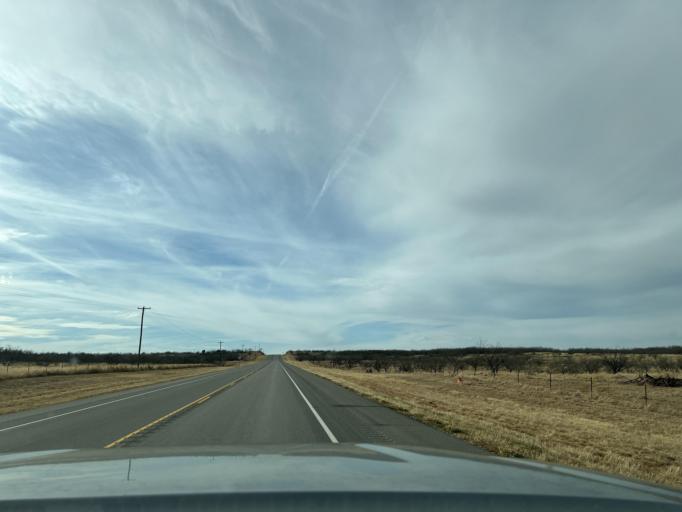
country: US
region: Texas
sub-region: Jones County
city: Anson
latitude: 32.7508
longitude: -99.7396
